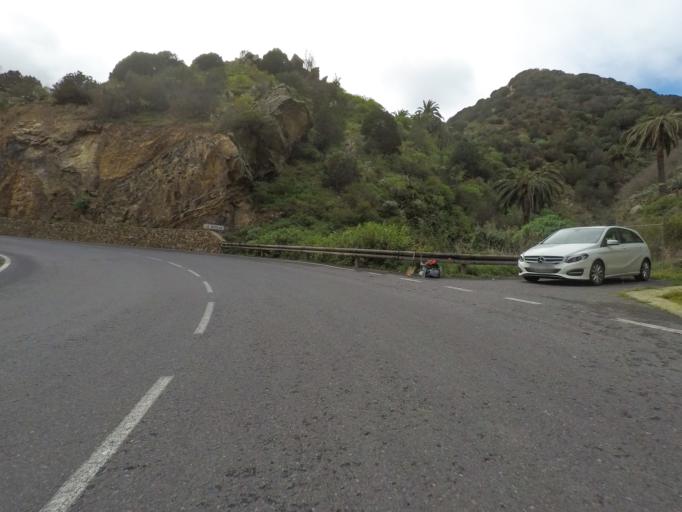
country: ES
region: Canary Islands
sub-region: Provincia de Santa Cruz de Tenerife
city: Vallehermosa
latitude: 28.1727
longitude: -17.2779
